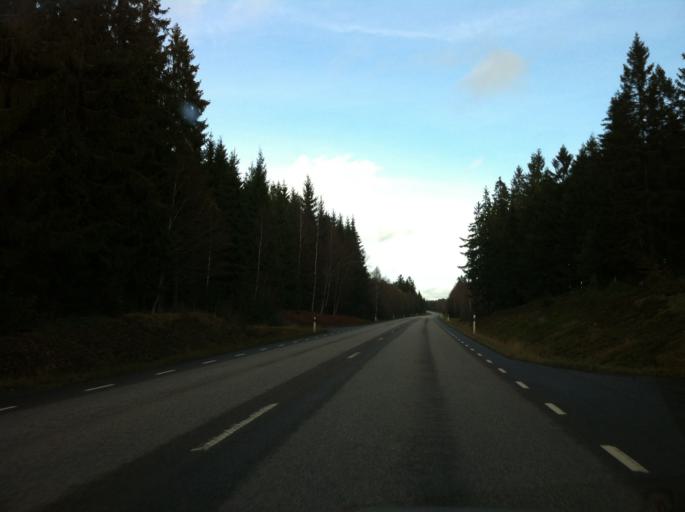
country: SE
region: Kronoberg
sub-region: Almhults Kommun
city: AElmhult
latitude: 56.5827
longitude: 14.1904
